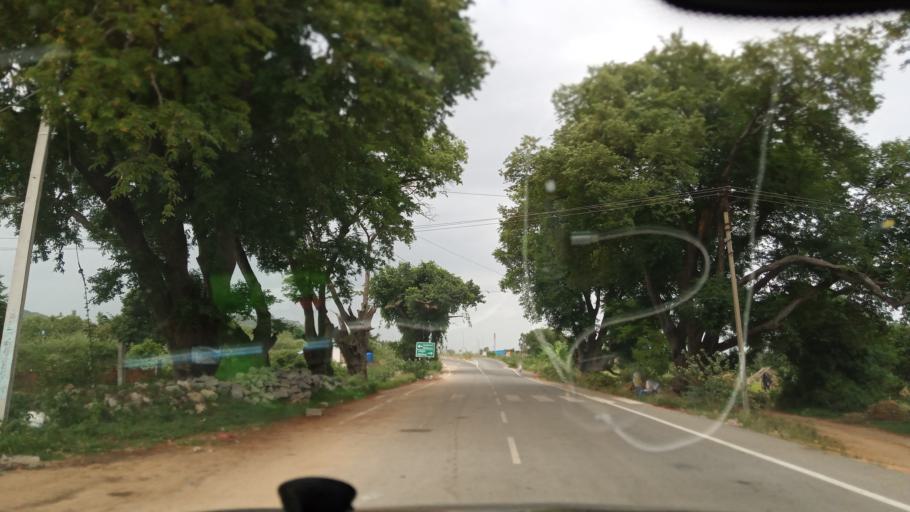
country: IN
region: Andhra Pradesh
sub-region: Chittoor
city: Palmaner
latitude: 13.1856
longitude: 78.8401
